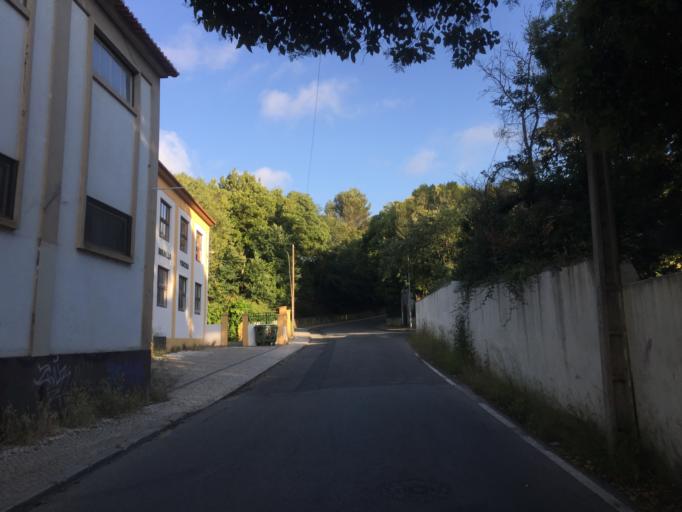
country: PT
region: Leiria
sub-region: Caldas da Rainha
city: Caldas da Rainha
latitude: 39.4003
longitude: -9.1306
